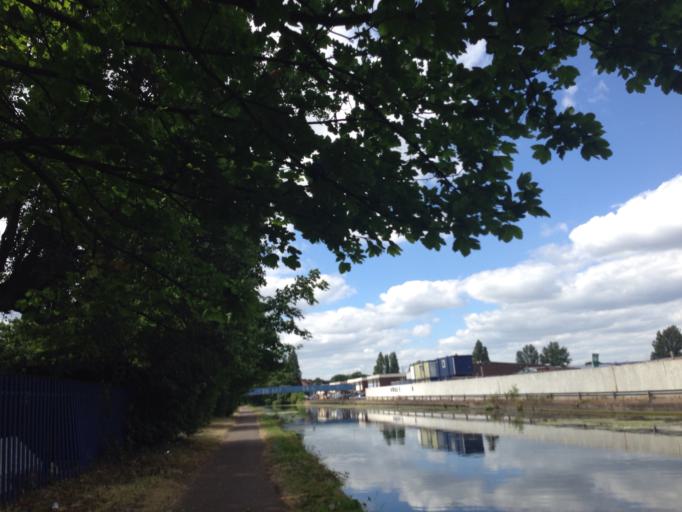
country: GB
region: England
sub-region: Greater London
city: Wembley
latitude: 51.5388
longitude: -0.2825
